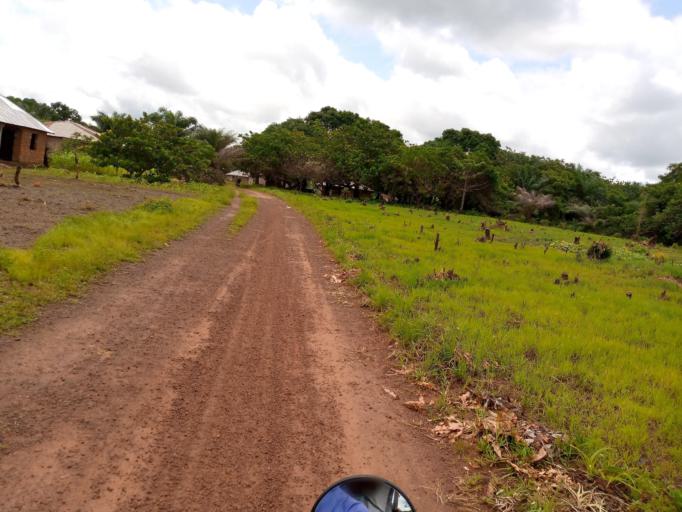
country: SL
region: Northern Province
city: Mange
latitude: 8.9911
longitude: -12.7825
